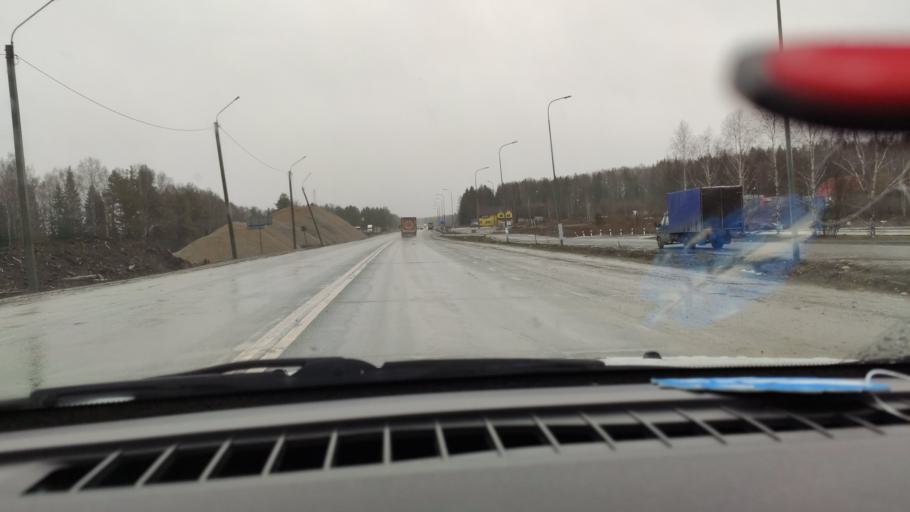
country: RU
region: Sverdlovsk
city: Bisert'
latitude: 56.8296
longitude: 59.0477
